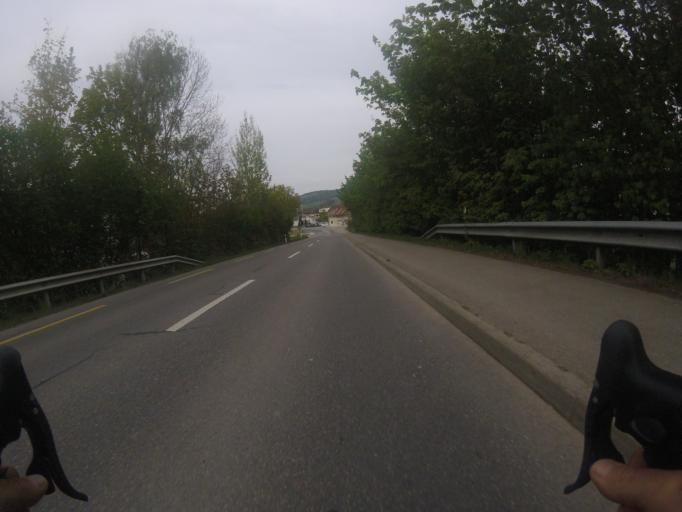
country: CH
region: Bern
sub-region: Bern-Mittelland District
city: Niederwichtrach
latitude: 46.8415
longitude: 7.5710
